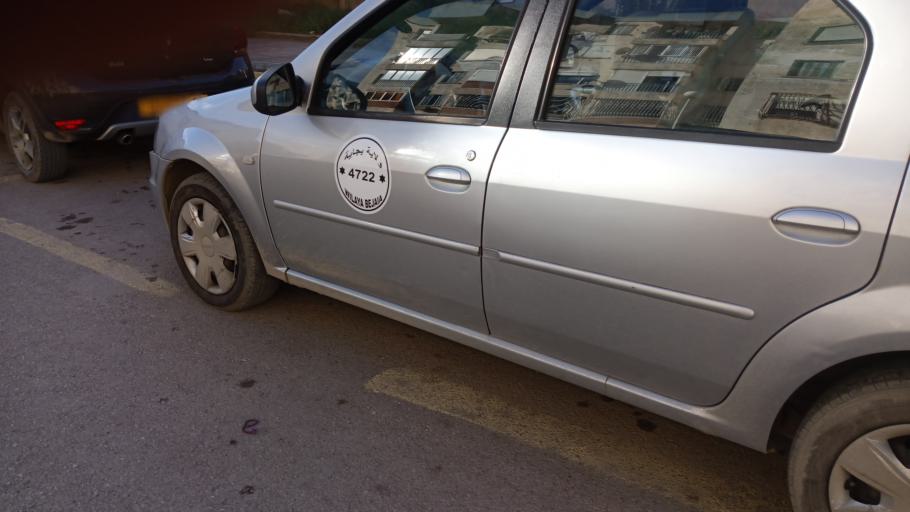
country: DZ
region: Bejaia
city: Bejaia
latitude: 36.7498
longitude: 5.0576
